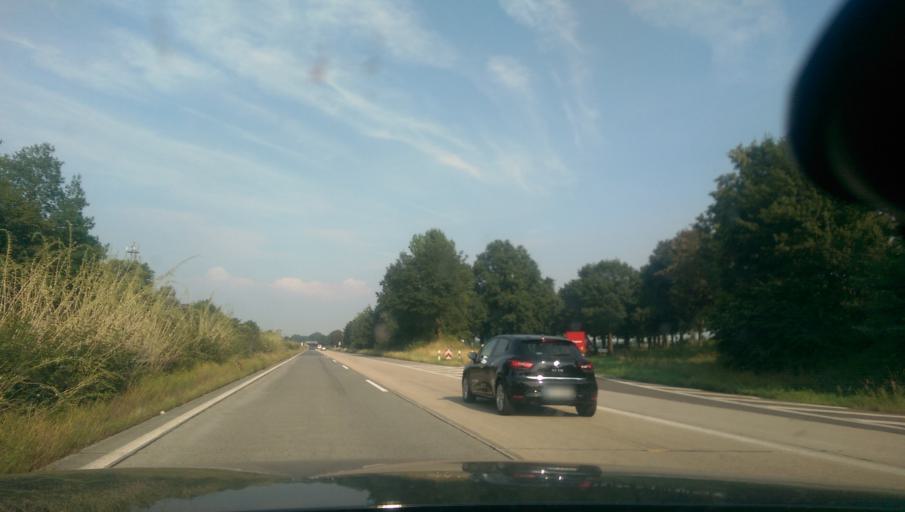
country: DE
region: North Rhine-Westphalia
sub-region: Regierungsbezirk Dusseldorf
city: Wachtendonk
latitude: 51.3891
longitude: 6.3138
